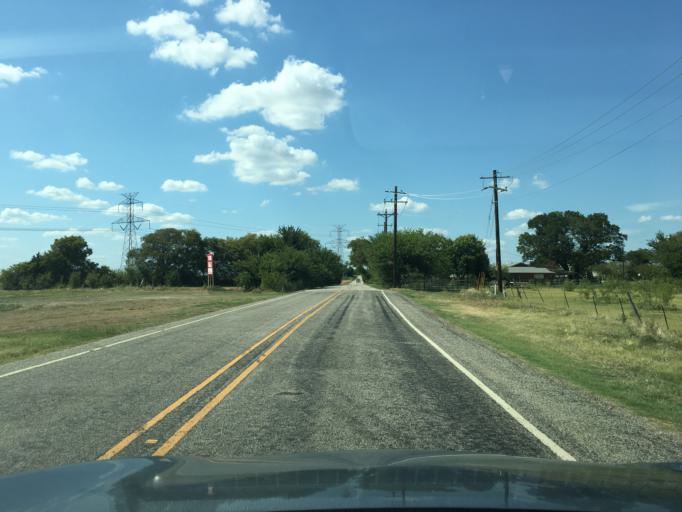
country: US
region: Texas
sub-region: Tarrant County
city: Mansfield
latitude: 32.5181
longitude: -97.0740
